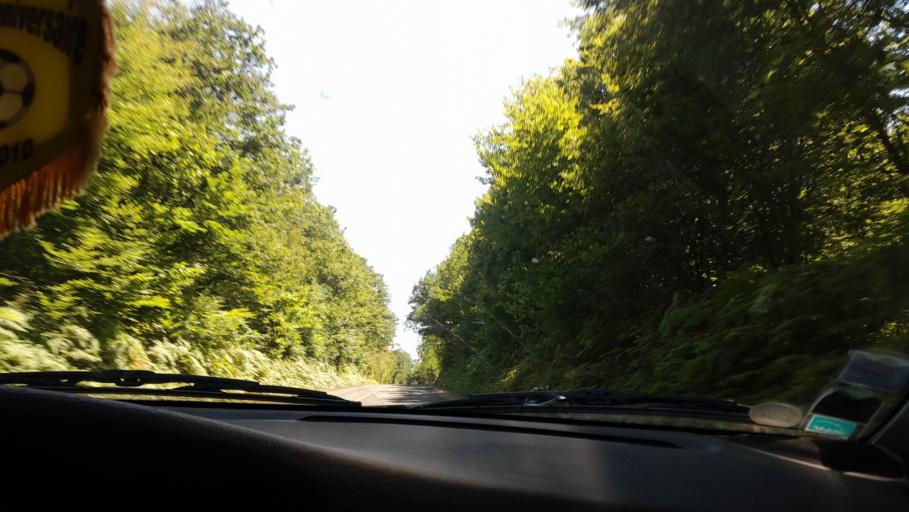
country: FR
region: Pays de la Loire
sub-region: Departement de Maine-et-Loire
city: Pouance
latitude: 47.7043
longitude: -1.1793
